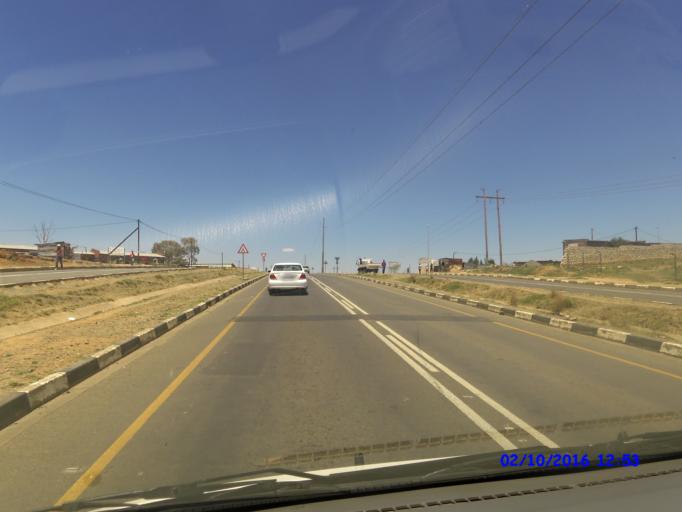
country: LS
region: Maseru
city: Maseru
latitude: -29.3590
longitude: 27.4616
